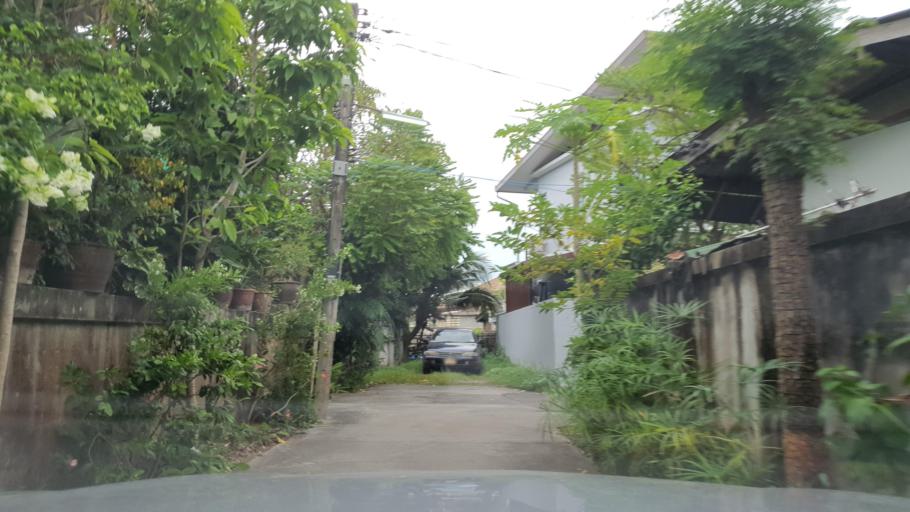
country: TH
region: Chiang Mai
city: San Sai
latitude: 18.9168
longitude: 98.9476
